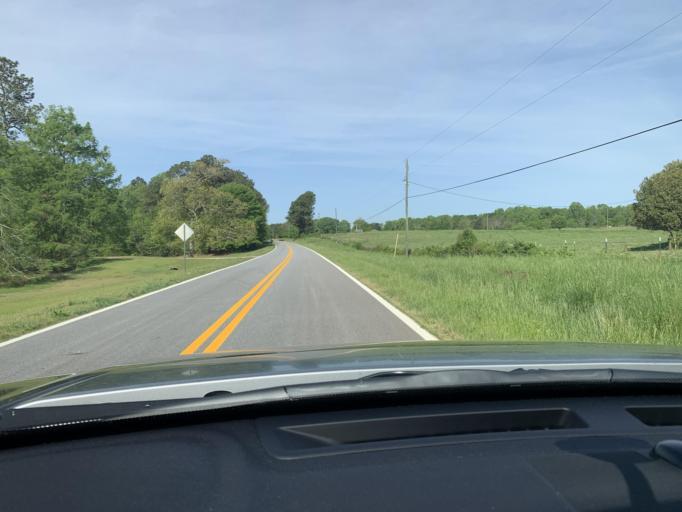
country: US
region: Georgia
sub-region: Oconee County
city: Watkinsville
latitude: 33.8181
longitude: -83.3659
